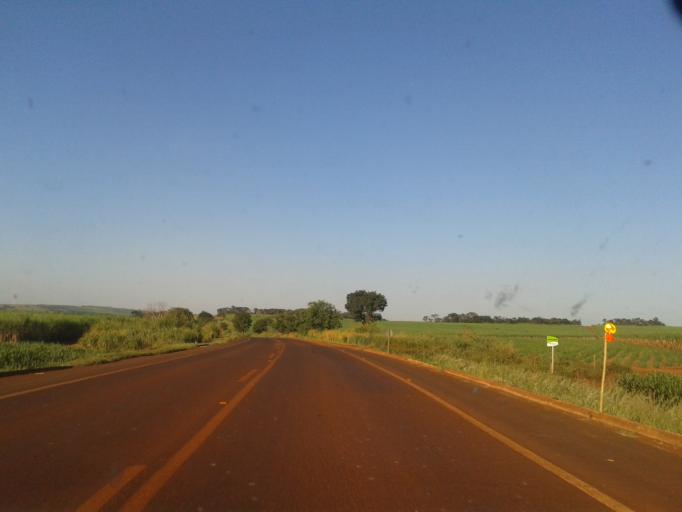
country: BR
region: Minas Gerais
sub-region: Capinopolis
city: Capinopolis
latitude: -18.6972
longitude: -49.6338
